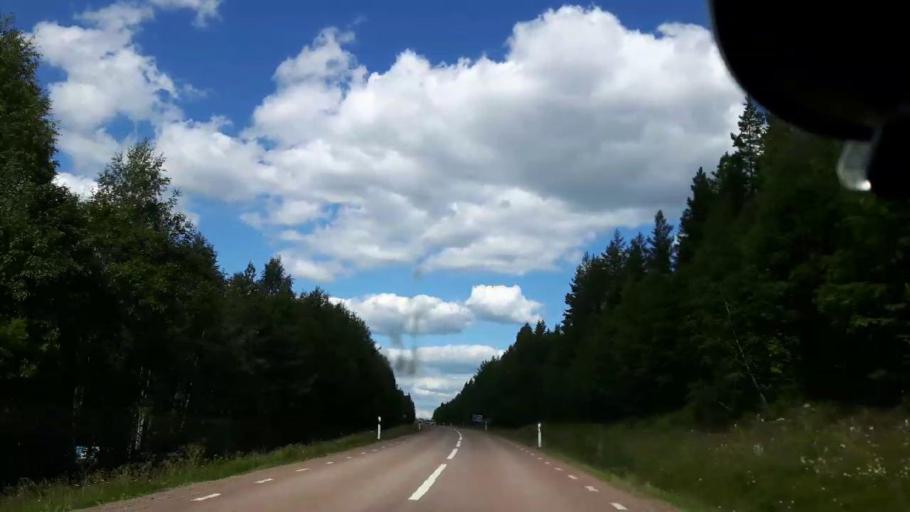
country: SE
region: Jaemtland
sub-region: Ragunda Kommun
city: Hammarstrand
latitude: 62.9226
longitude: 16.7030
